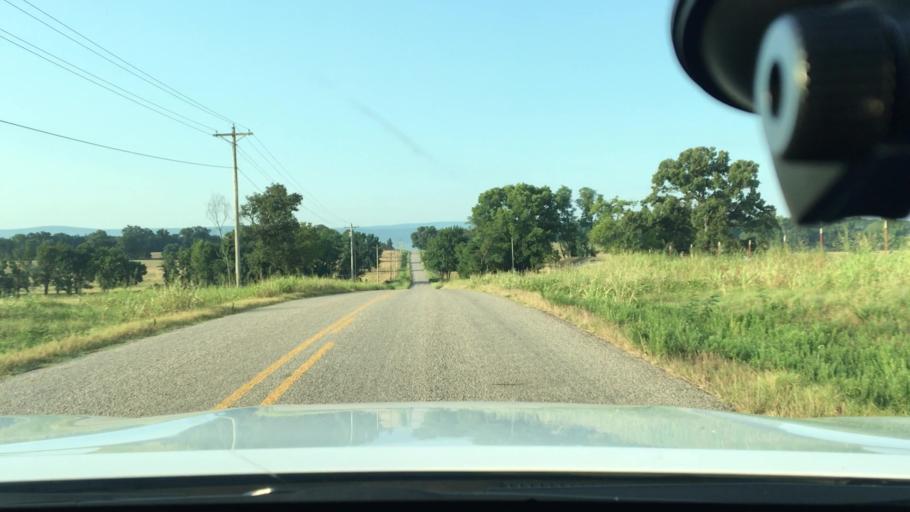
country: US
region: Arkansas
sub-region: Johnson County
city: Coal Hill
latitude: 35.3574
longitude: -93.6132
